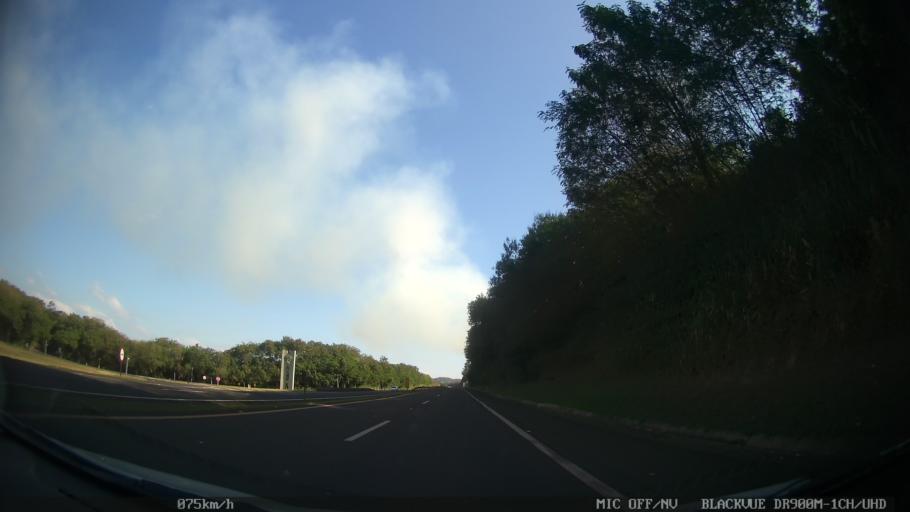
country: BR
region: Sao Paulo
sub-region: Piracicaba
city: Piracicaba
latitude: -22.6884
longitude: -47.5846
